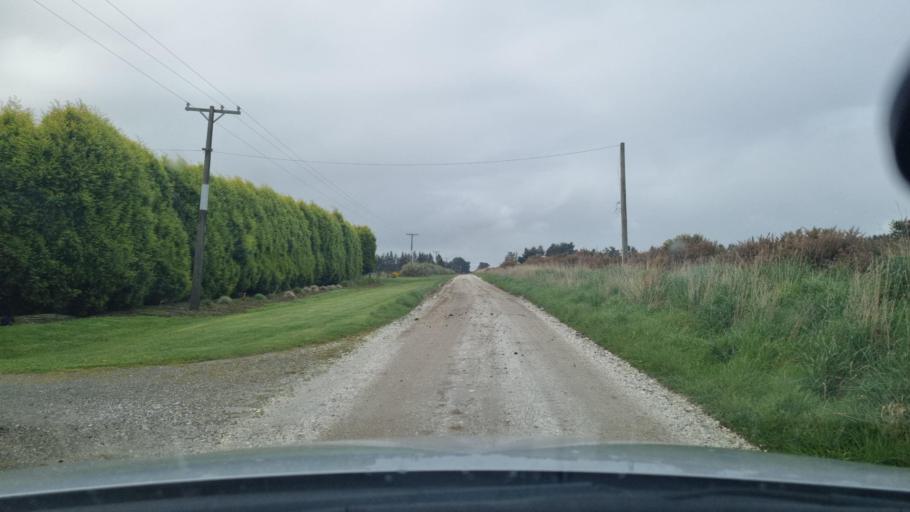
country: NZ
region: Southland
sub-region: Invercargill City
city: Invercargill
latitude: -46.4956
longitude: 168.4203
